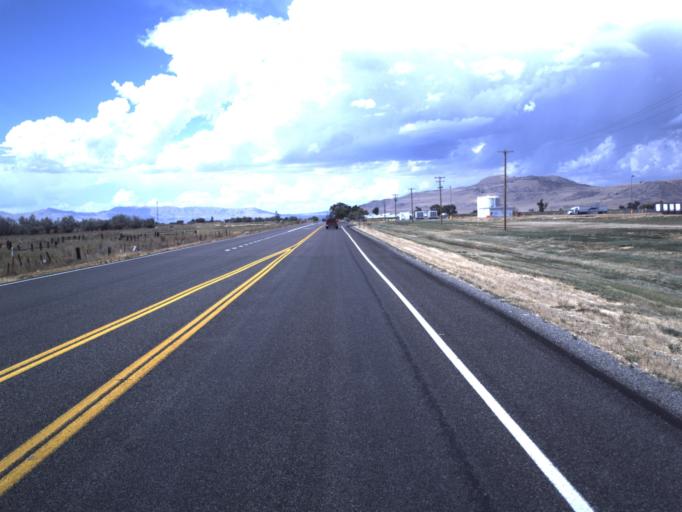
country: US
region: Utah
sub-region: Box Elder County
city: Honeyville
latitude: 41.5582
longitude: -112.1434
